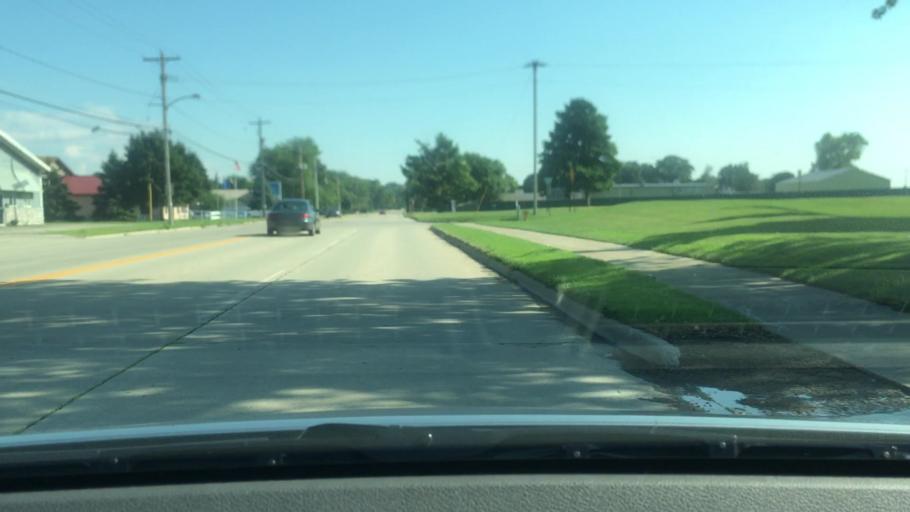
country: US
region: Wisconsin
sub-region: Winnebago County
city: Oshkosh
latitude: 43.9845
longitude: -88.5426
